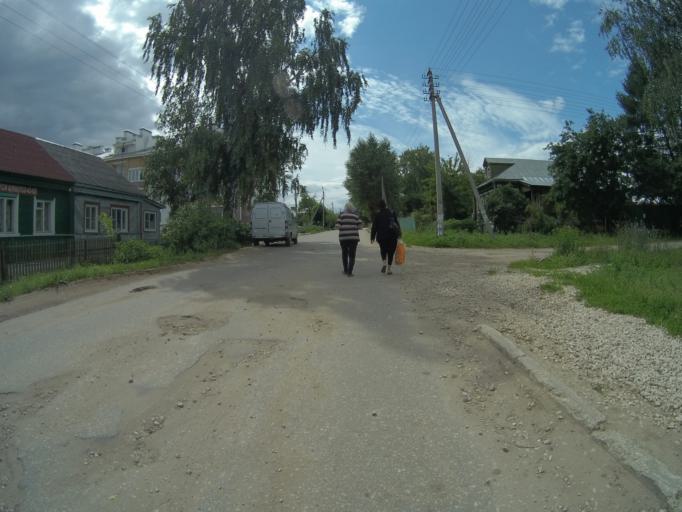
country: RU
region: Vladimir
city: Bogolyubovo
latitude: 56.1985
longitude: 40.5324
